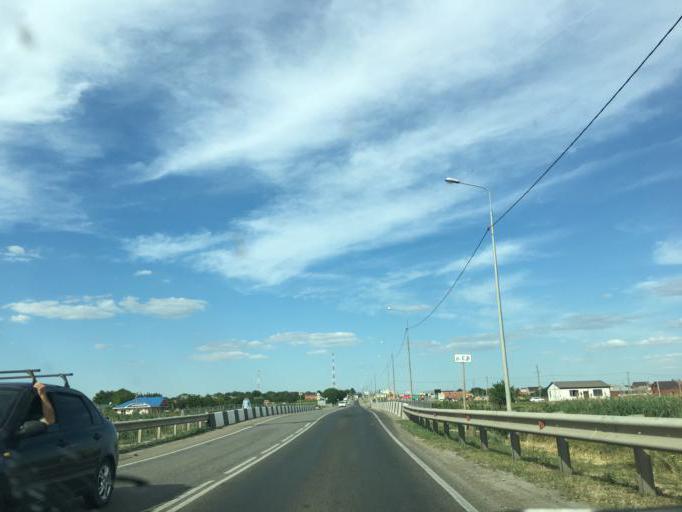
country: RU
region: Krasnodarskiy
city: Kushchevskaya
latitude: 46.5531
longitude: 39.6550
